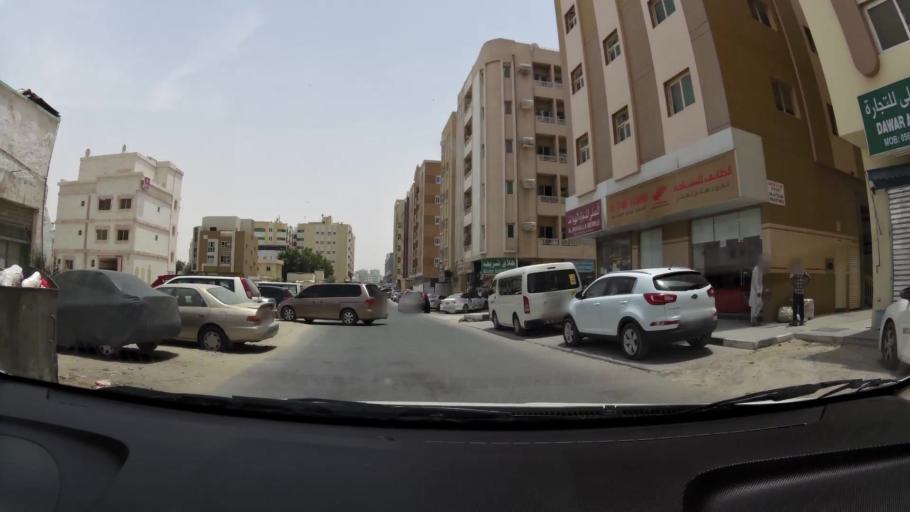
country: AE
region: Ash Shariqah
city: Sharjah
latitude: 25.3562
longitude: 55.3951
